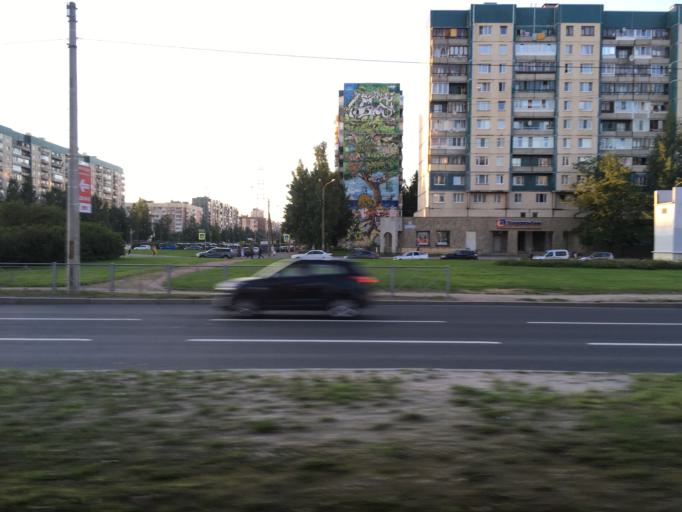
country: RU
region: St.-Petersburg
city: Komendantsky aerodrom
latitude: 60.0071
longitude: 30.2667
